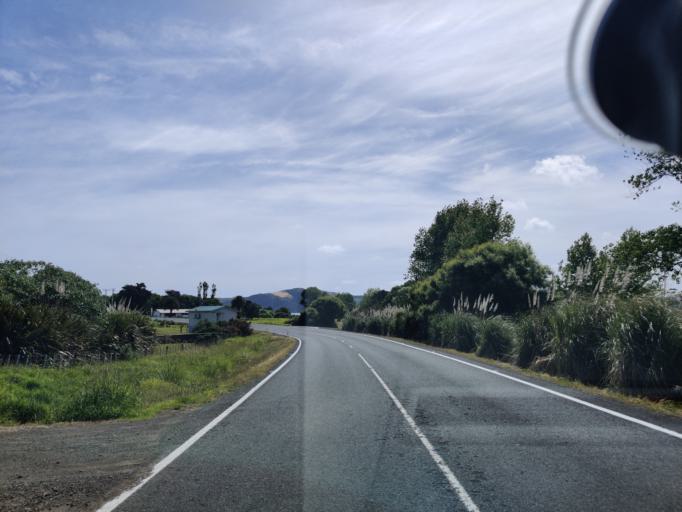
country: NZ
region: Northland
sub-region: Far North District
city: Kaitaia
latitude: -35.4959
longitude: 173.4126
